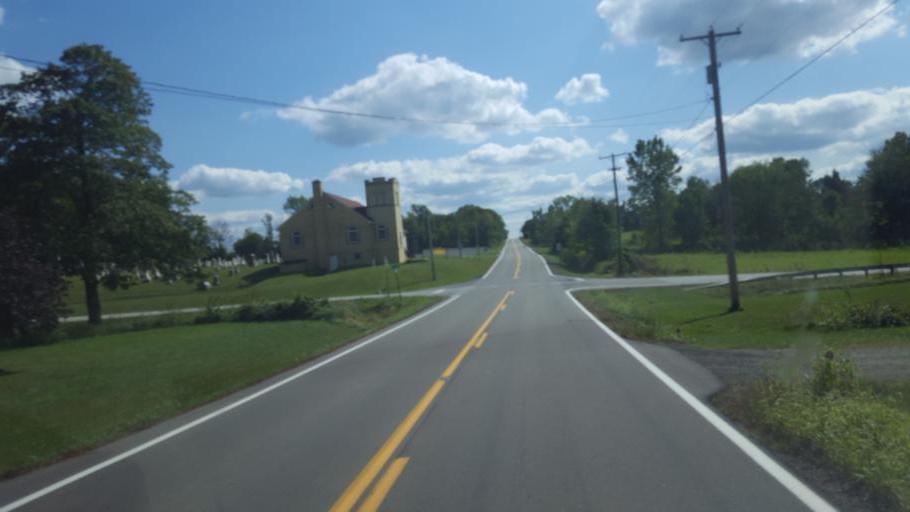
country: US
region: Ohio
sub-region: Ashland County
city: Ashland
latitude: 40.8718
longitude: -82.2117
